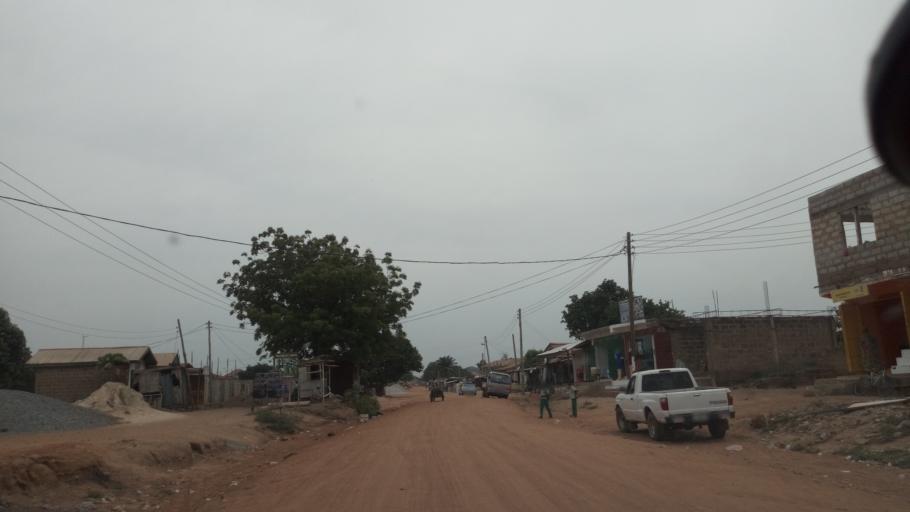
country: GH
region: Greater Accra
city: Medina Estates
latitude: 5.7060
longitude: -0.1329
